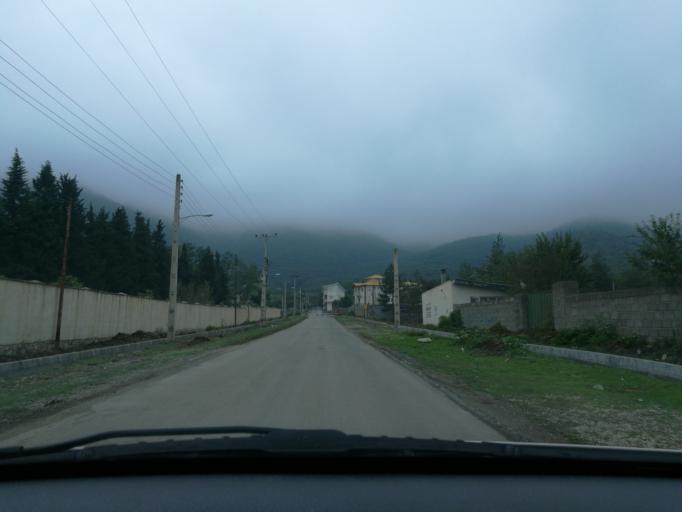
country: IR
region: Mazandaran
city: `Abbasabad
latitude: 36.4997
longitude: 51.2153
